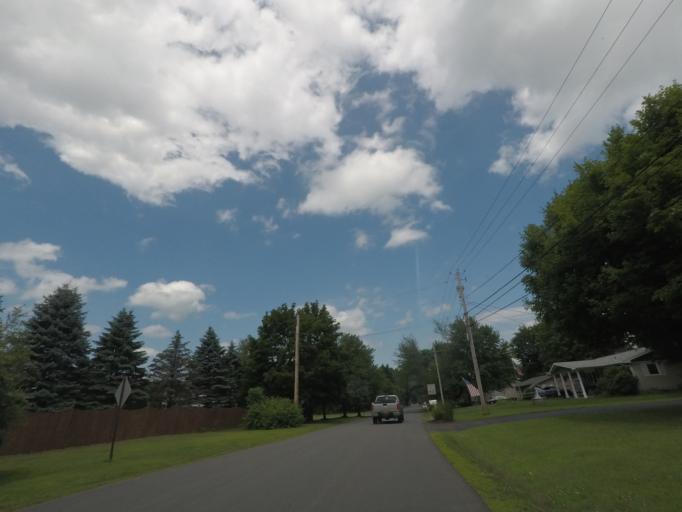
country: US
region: New York
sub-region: Rensselaer County
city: Castleton-on-Hudson
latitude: 42.5283
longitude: -73.6908
